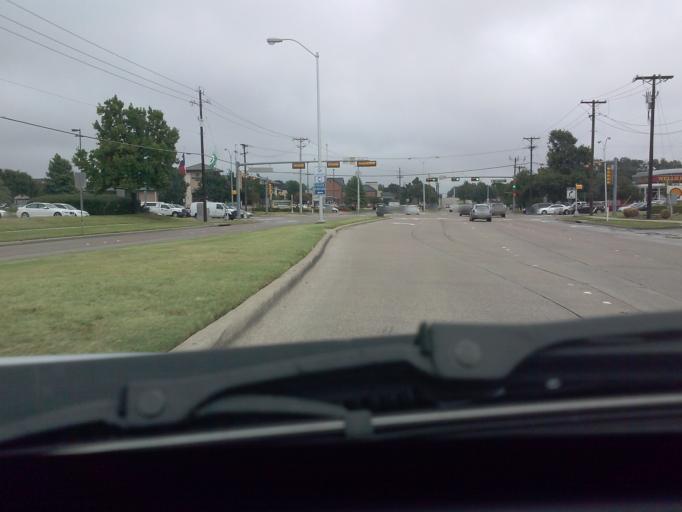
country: US
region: Texas
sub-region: Collin County
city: Plano
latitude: 33.0718
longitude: -96.7512
